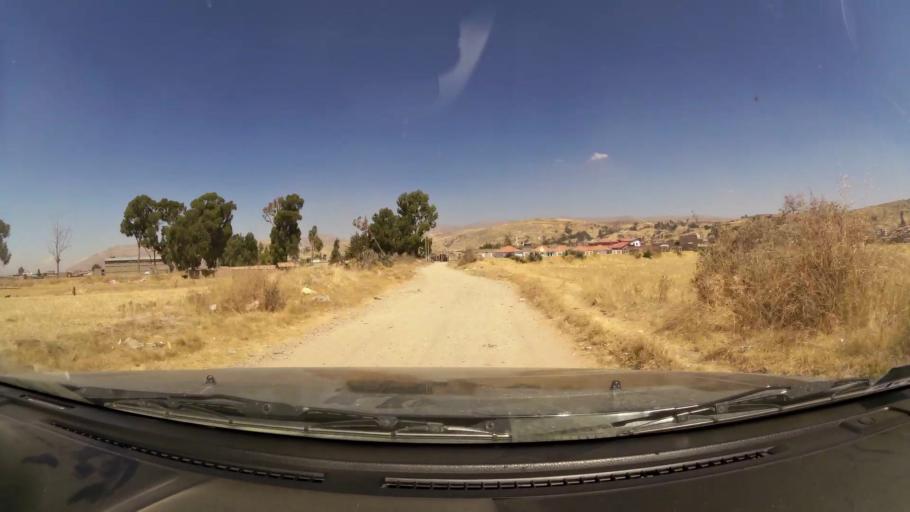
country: PE
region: Junin
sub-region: Provincia de Jauja
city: Jauja
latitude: -11.7654
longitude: -75.4966
